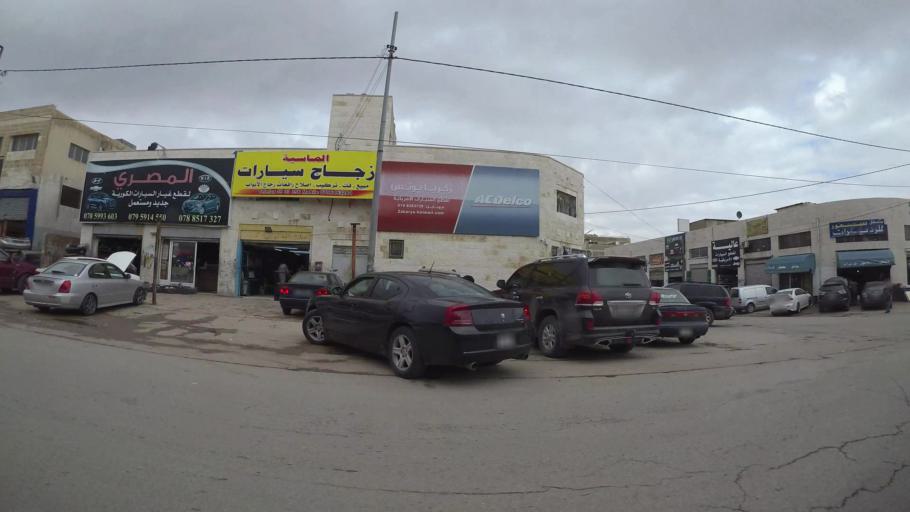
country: JO
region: Amman
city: Wadi as Sir
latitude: 31.9437
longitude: 35.8386
